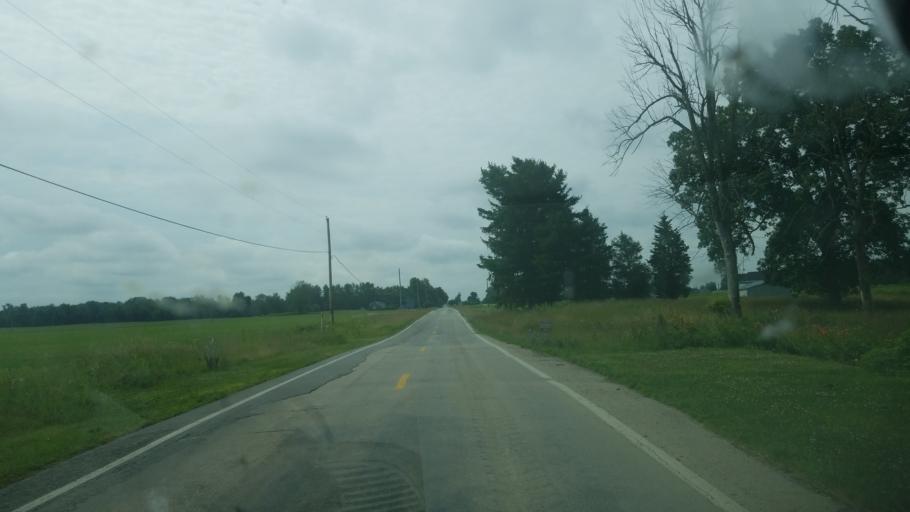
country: US
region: Ohio
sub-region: Licking County
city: Johnstown
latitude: 40.1486
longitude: -82.7601
